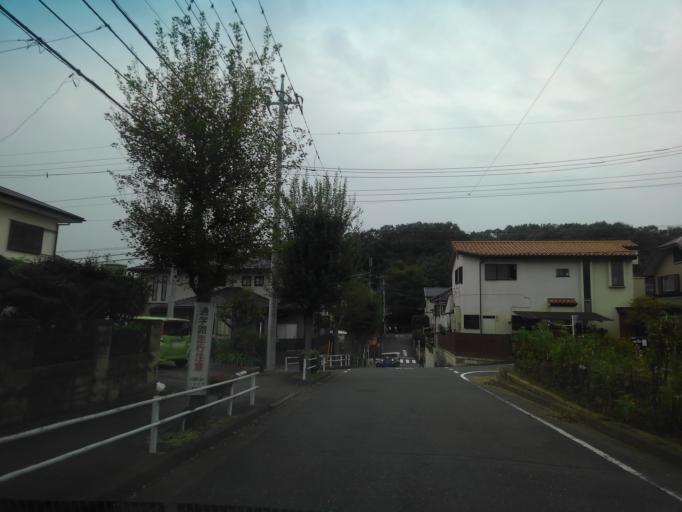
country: JP
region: Tokyo
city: Hachioji
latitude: 35.6896
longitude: 139.3514
